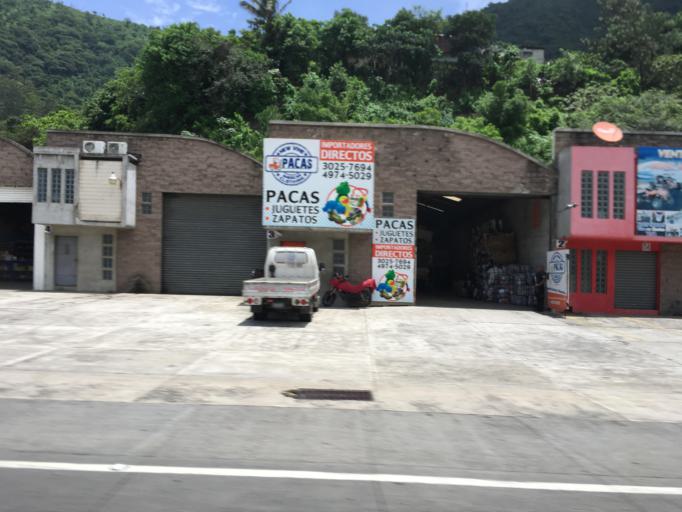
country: GT
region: Escuintla
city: San Vicente Pacaya
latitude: 14.4325
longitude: -90.6563
